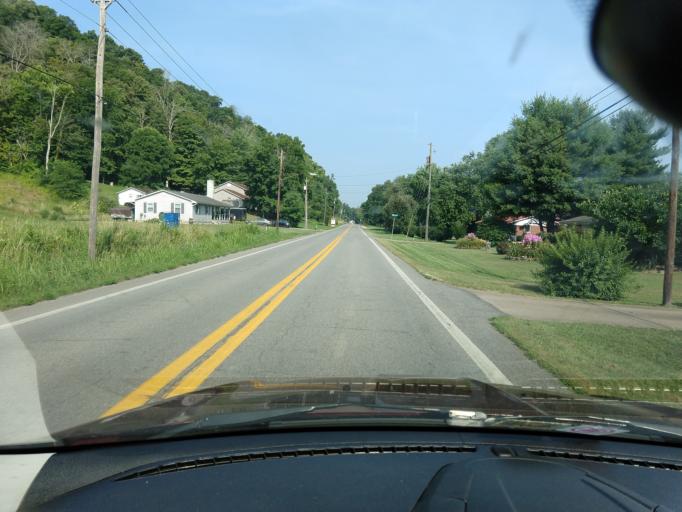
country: US
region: West Virginia
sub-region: Mason County
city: New Haven
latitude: 38.9835
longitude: -81.9540
